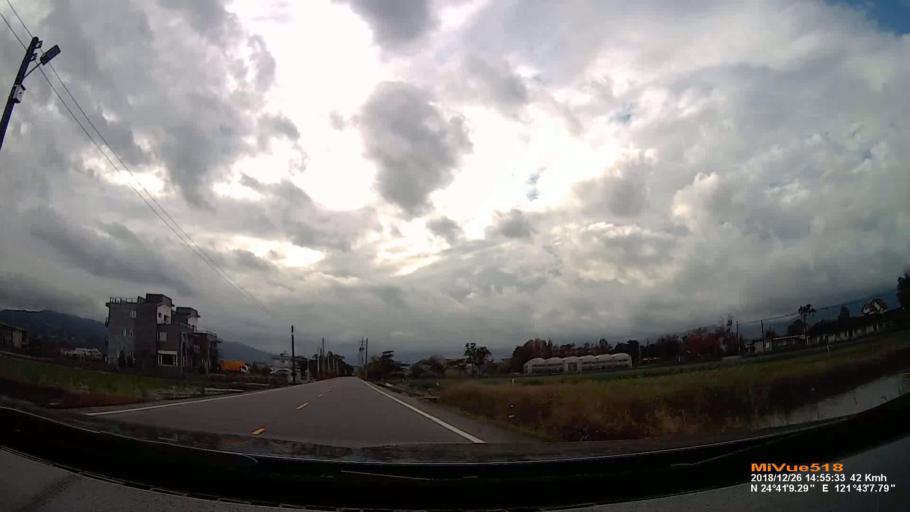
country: TW
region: Taiwan
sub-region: Yilan
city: Yilan
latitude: 24.6859
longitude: 121.7187
